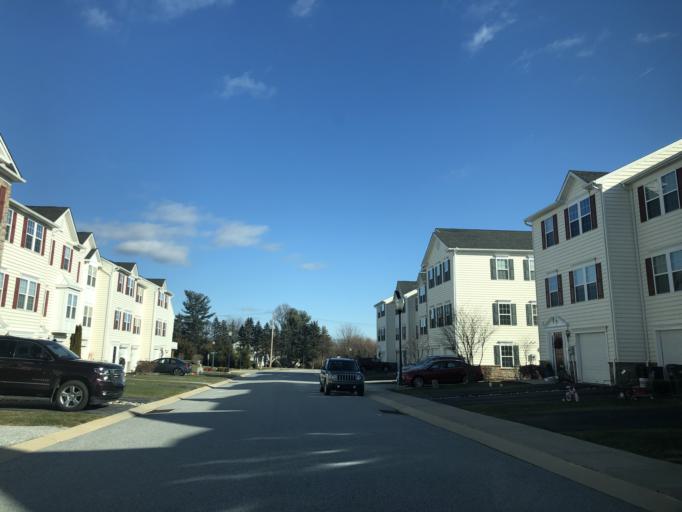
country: US
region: Pennsylvania
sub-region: Chester County
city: Parkesburg
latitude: 39.9847
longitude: -75.8764
